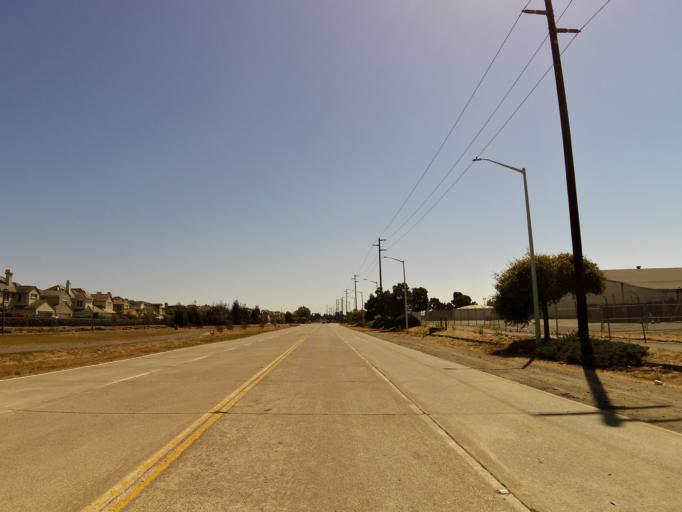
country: US
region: California
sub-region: Alameda County
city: Oakland
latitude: 37.7831
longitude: -122.2914
